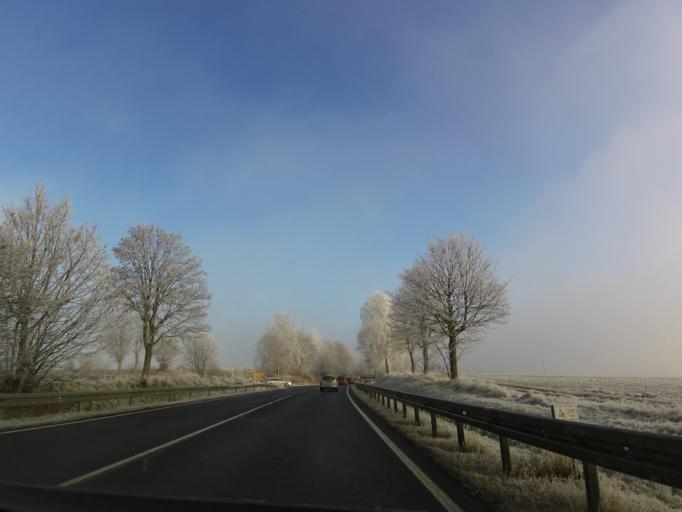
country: DE
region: Bavaria
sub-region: Upper Franconia
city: Arzberg
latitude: 50.0734
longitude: 12.1895
